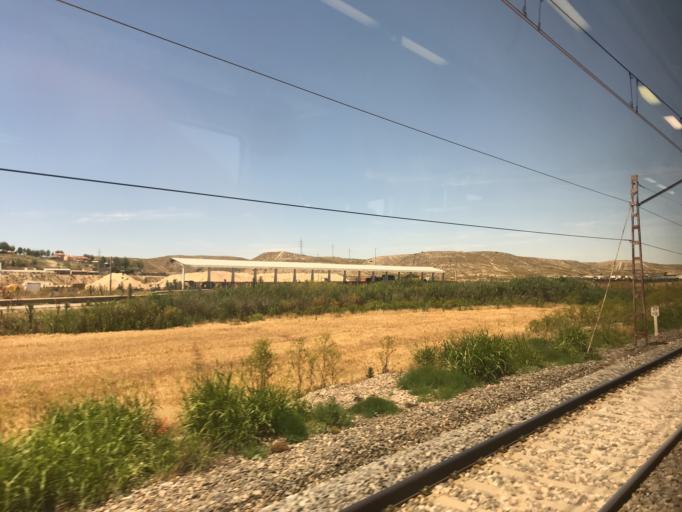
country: ES
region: Madrid
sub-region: Provincia de Madrid
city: Ciempozuelos
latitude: 40.1096
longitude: -3.6233
